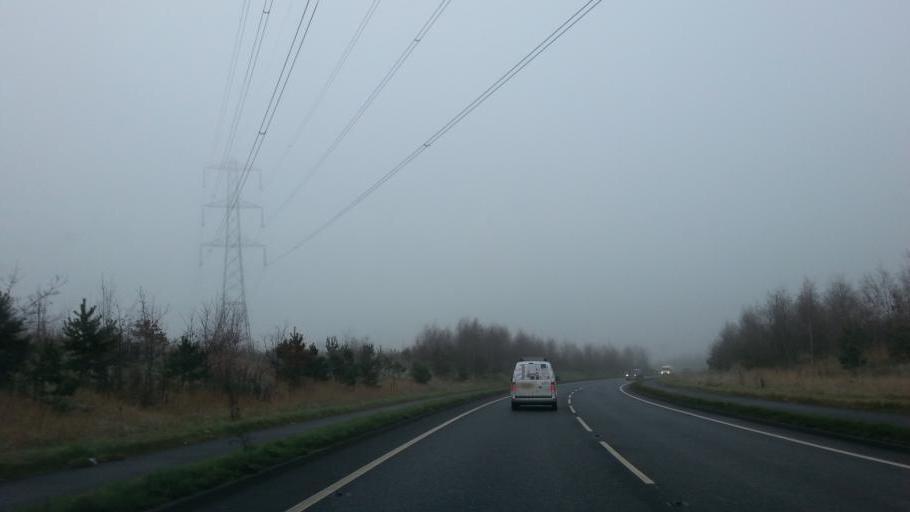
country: GB
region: England
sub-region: Cheshire East
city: Alderley Edge
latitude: 53.2928
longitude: -2.2558
